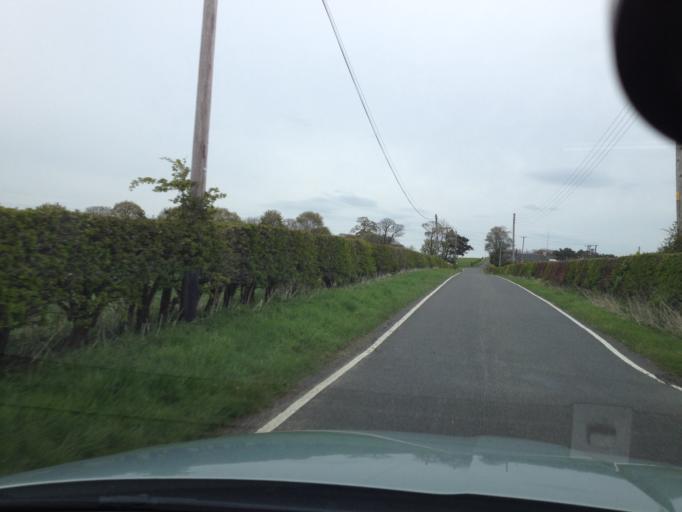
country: GB
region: Scotland
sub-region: West Lothian
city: Livingston
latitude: 55.9312
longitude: -3.5506
